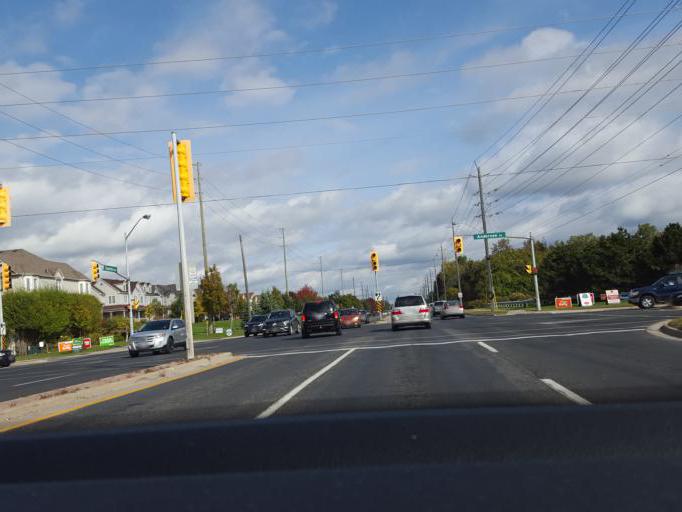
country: CA
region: Ontario
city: Oshawa
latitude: 43.9196
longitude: -78.9379
